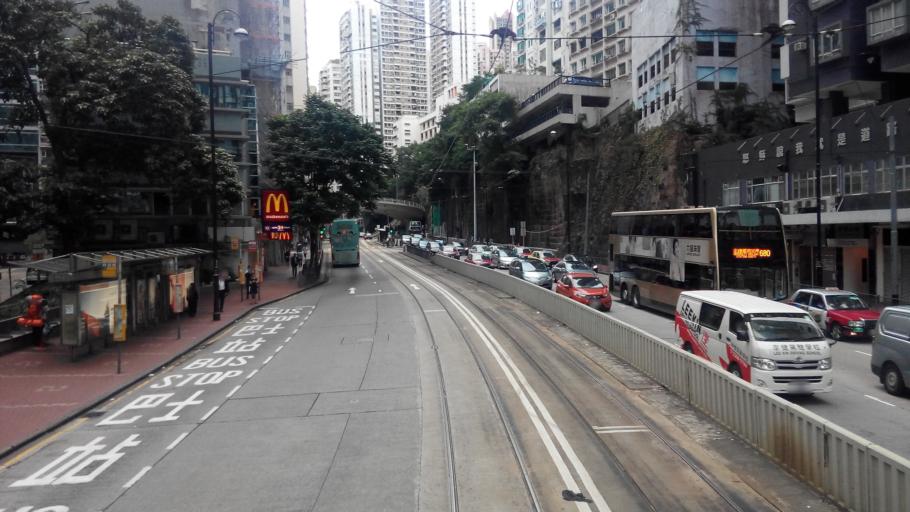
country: HK
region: Wanchai
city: Wan Chai
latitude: 22.2834
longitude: 114.1925
